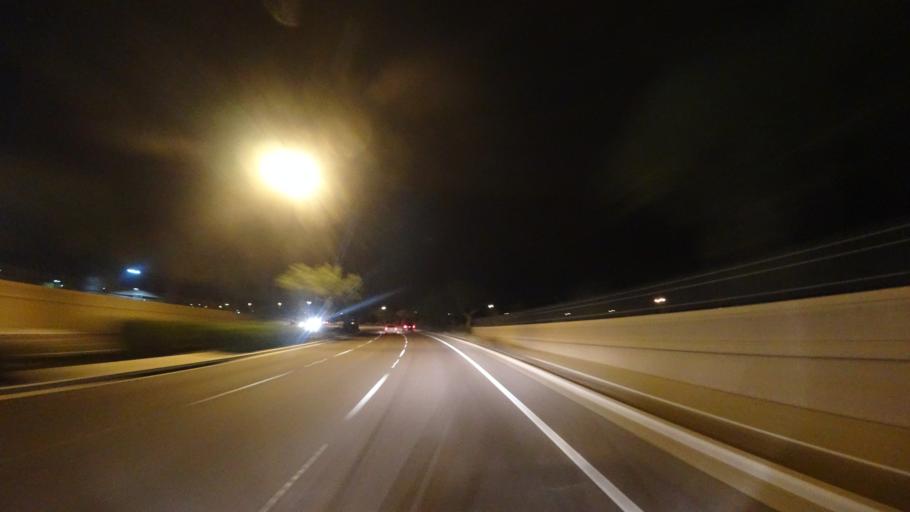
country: US
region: Arizona
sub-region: Maricopa County
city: Gilbert
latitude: 33.3249
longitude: -111.7398
